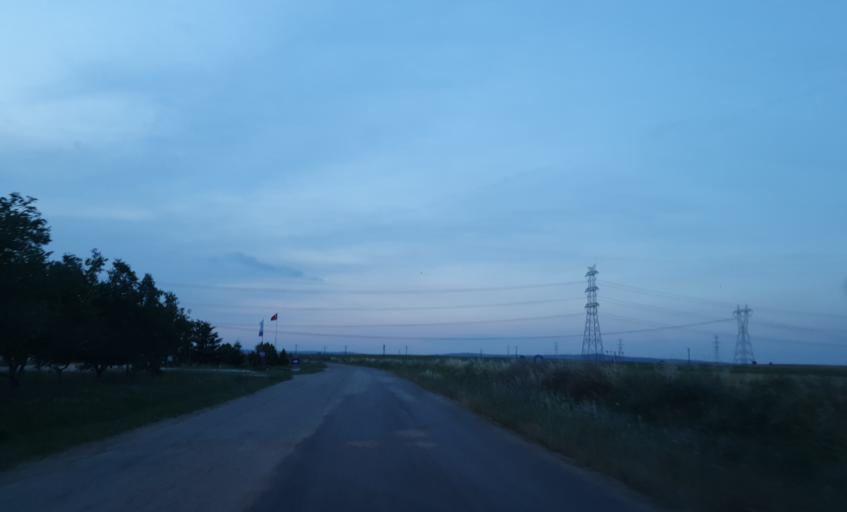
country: TR
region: Kirklareli
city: Vize
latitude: 41.4920
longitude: 27.7517
